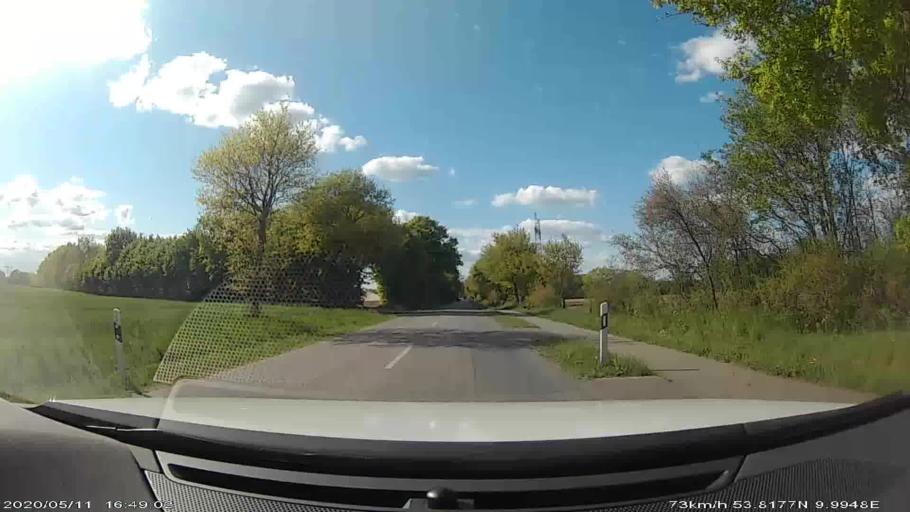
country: DE
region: Schleswig-Holstein
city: Oersdorf
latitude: 53.8239
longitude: 9.9863
